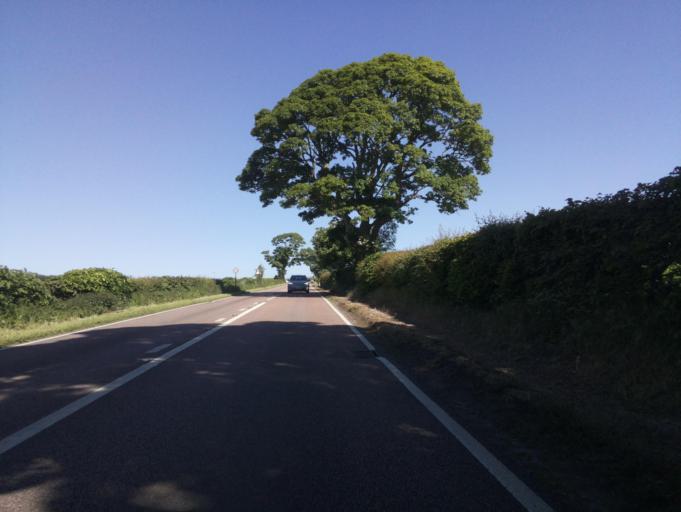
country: GB
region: Scotland
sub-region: Fife
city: Newport-On-Tay
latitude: 56.4247
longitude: -2.9232
